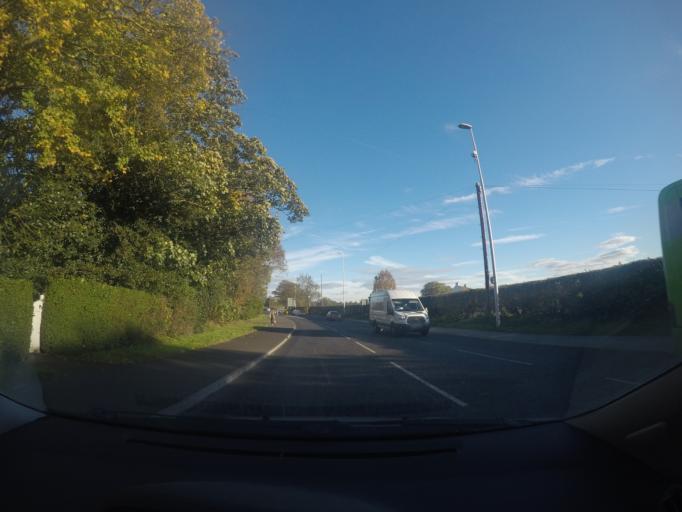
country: GB
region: England
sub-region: City of York
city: Nether Poppleton
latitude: 53.9723
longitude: -1.1422
